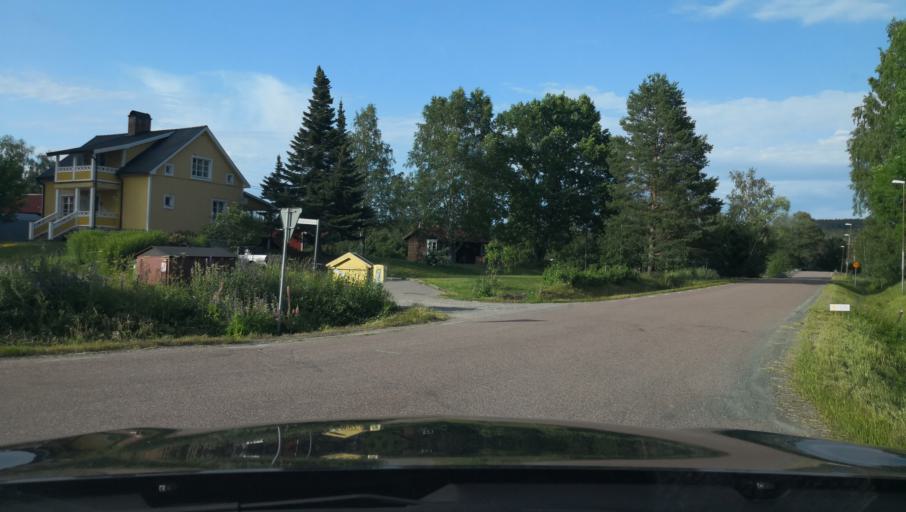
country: SE
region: Dalarna
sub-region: Ludvika Kommun
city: Ludvika
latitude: 60.0748
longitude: 15.2492
